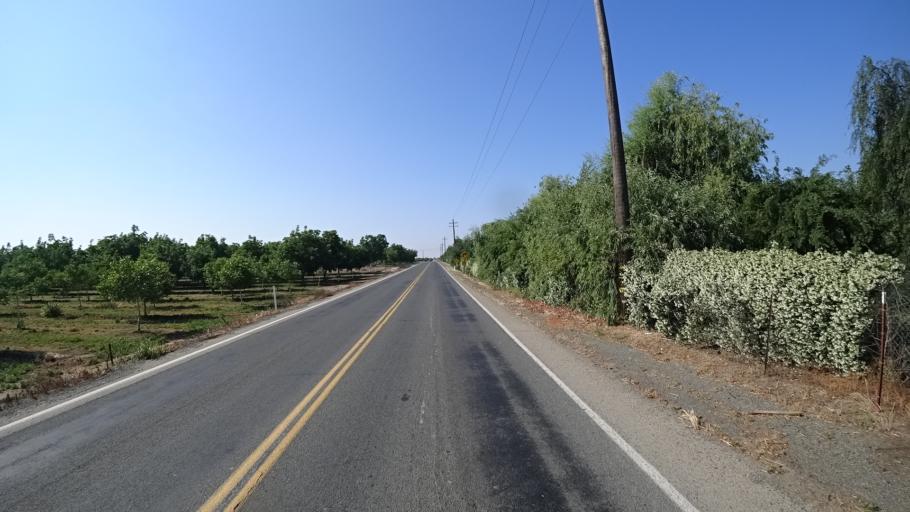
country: US
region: California
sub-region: Fresno County
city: Kingsburg
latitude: 36.4841
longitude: -119.5573
